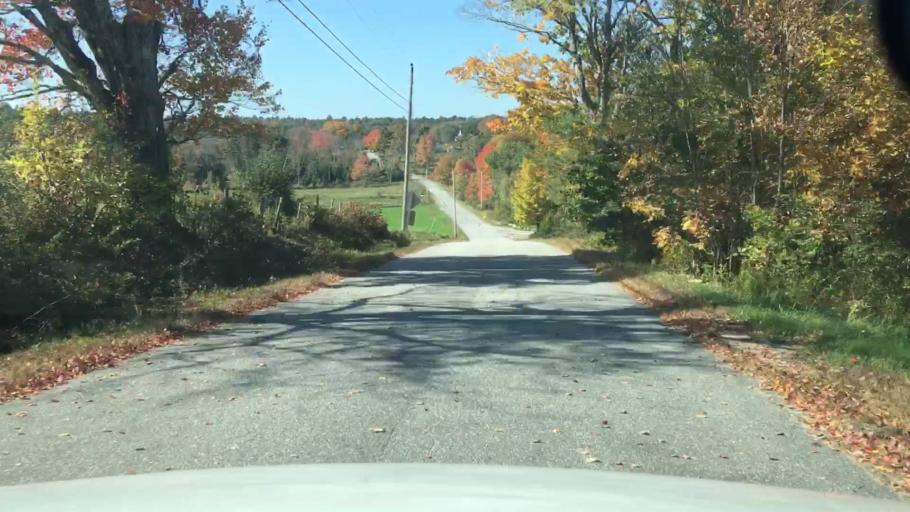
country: US
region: Maine
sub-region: Sagadahoc County
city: Topsham
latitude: 44.0125
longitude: -69.9617
